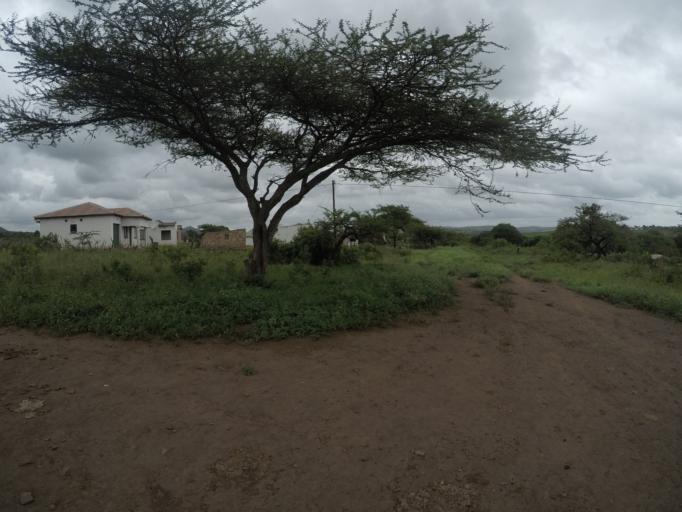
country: ZA
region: KwaZulu-Natal
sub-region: uThungulu District Municipality
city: Empangeni
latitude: -28.5691
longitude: 31.8710
